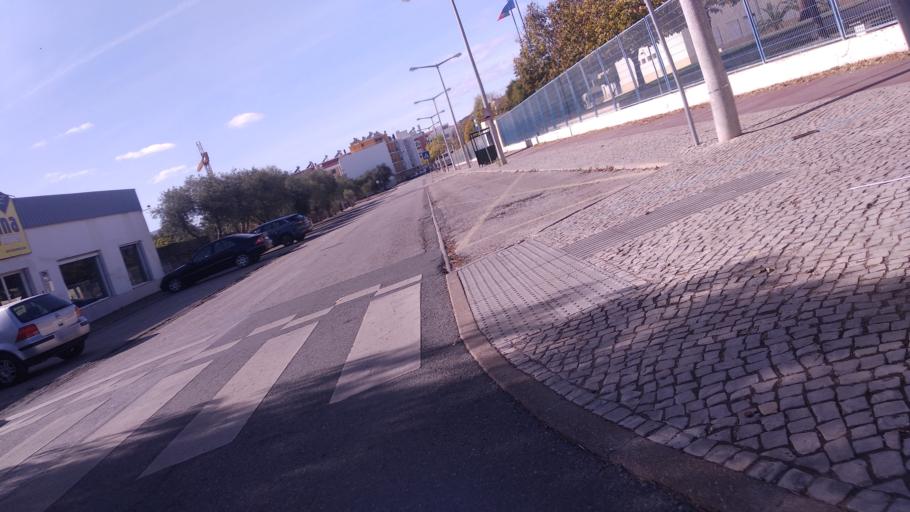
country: PT
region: Faro
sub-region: Sao Bras de Alportel
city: Sao Bras de Alportel
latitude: 37.1569
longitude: -7.8855
